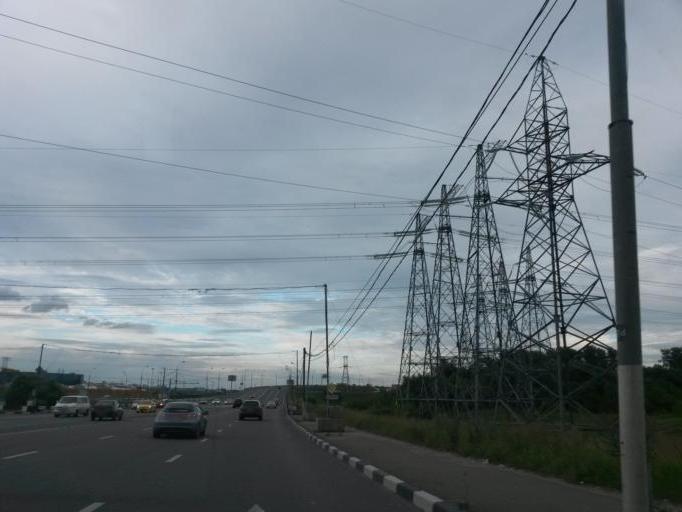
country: RU
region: Moscow
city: Zyablikovo
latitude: 55.6190
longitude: 37.7732
